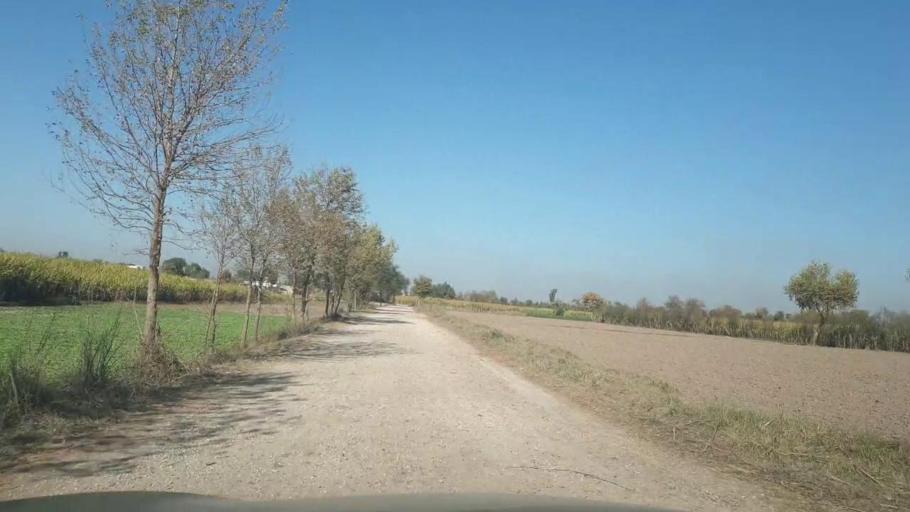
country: PK
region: Sindh
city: Mirpur Mathelo
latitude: 28.0787
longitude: 69.4898
